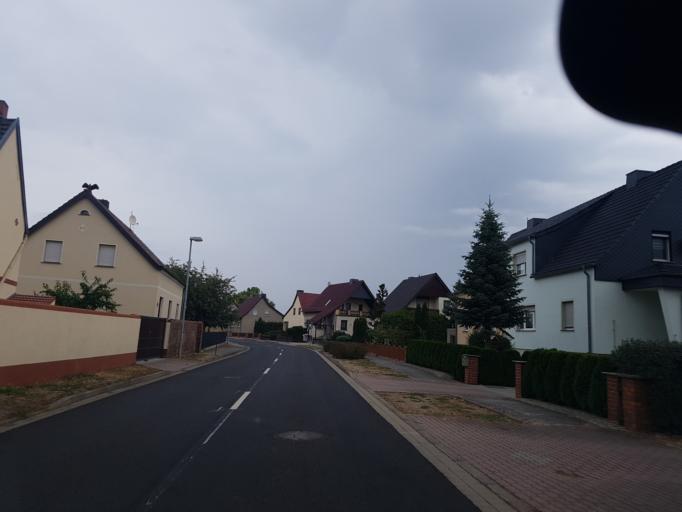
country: DE
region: Saxony-Anhalt
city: Jessen
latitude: 51.7661
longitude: 12.9058
